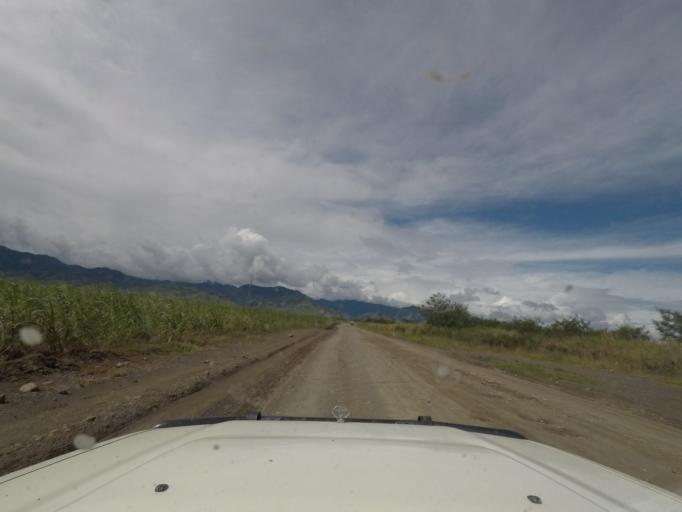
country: PG
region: Eastern Highlands
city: Kainantu
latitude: -6.0287
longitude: 145.9343
